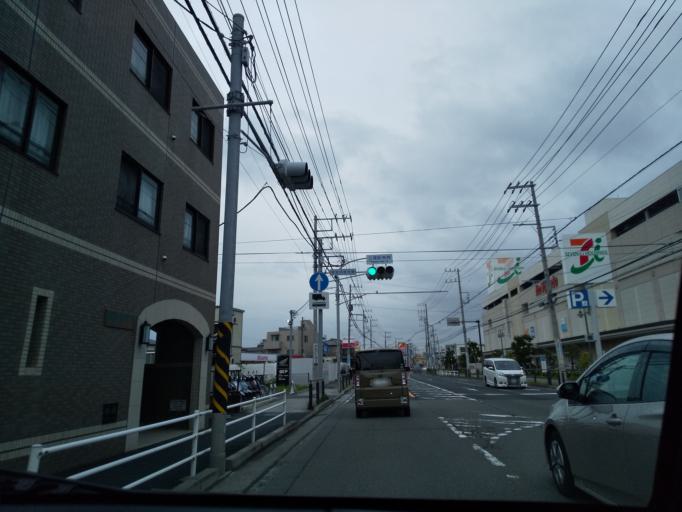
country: JP
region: Kanagawa
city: Fujisawa
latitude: 35.4123
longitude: 139.4999
